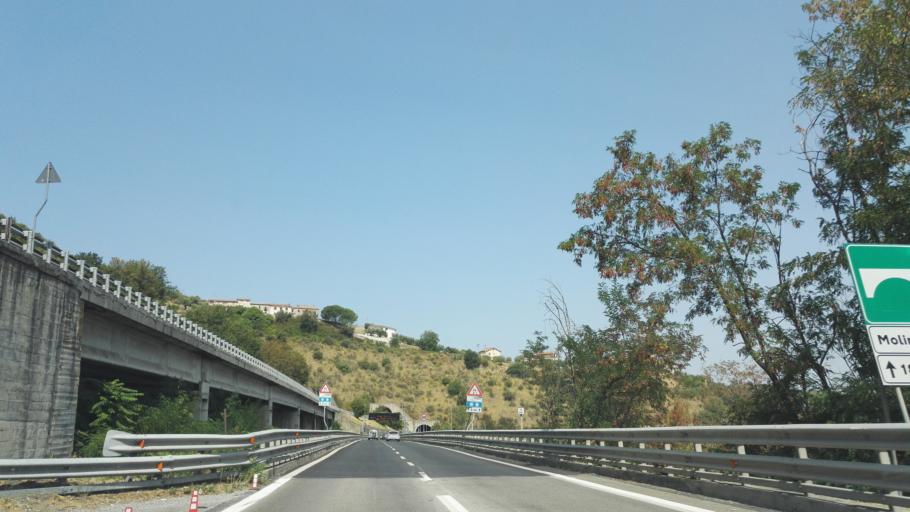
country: IT
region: Calabria
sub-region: Provincia di Cosenza
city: Laurignano
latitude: 39.2812
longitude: 16.2469
